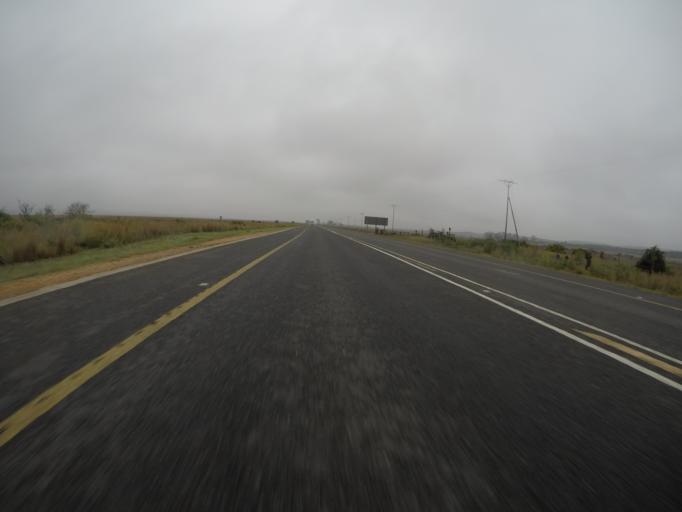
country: ZA
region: Western Cape
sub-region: Eden District Municipality
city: Riversdale
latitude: -34.1703
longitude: 21.3252
